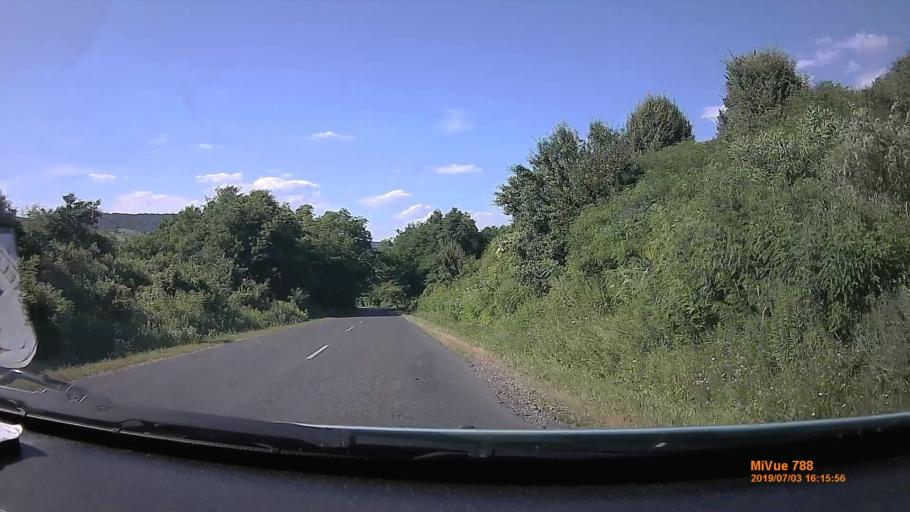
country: HU
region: Borsod-Abauj-Zemplen
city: Putnok
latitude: 48.2037
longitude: 20.4917
